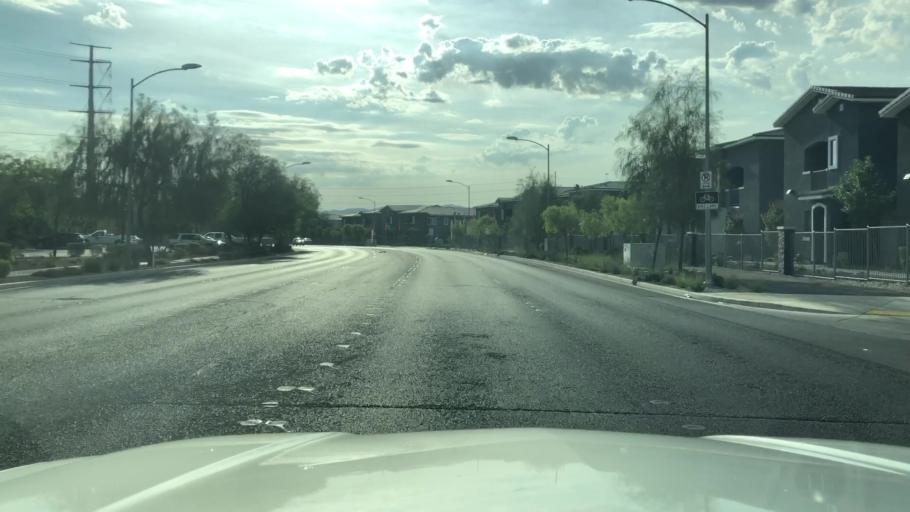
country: US
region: Nevada
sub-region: Clark County
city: Henderson
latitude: 36.0333
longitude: -115.0346
